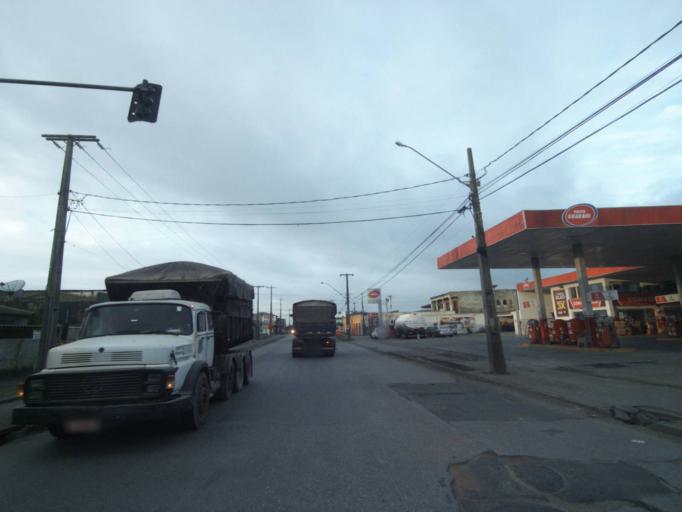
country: BR
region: Parana
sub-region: Paranagua
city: Paranagua
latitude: -25.5178
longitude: -48.5410
